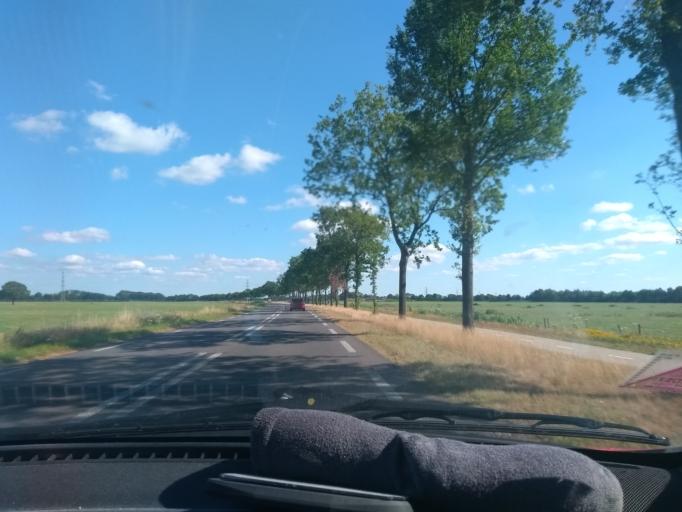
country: NL
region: Drenthe
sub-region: Gemeente Tynaarlo
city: Vries
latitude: 53.1253
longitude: 6.5026
